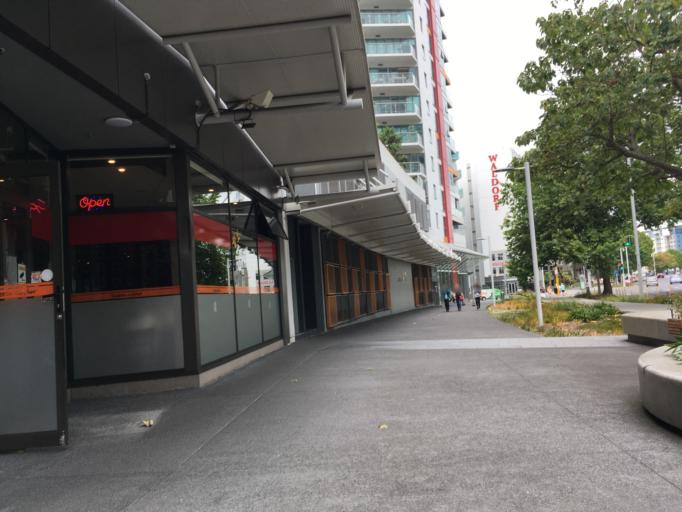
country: NZ
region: Auckland
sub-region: Auckland
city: Auckland
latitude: -36.8458
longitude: 174.7723
